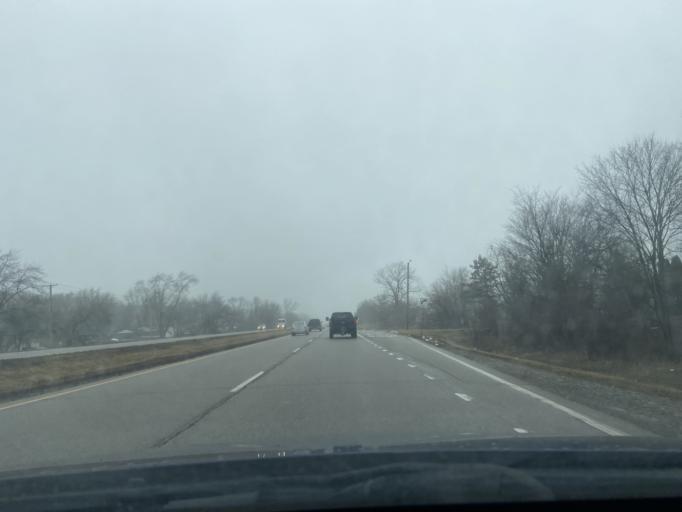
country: US
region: Illinois
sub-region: Lake County
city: Wauconda
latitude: 42.2676
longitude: -88.1545
